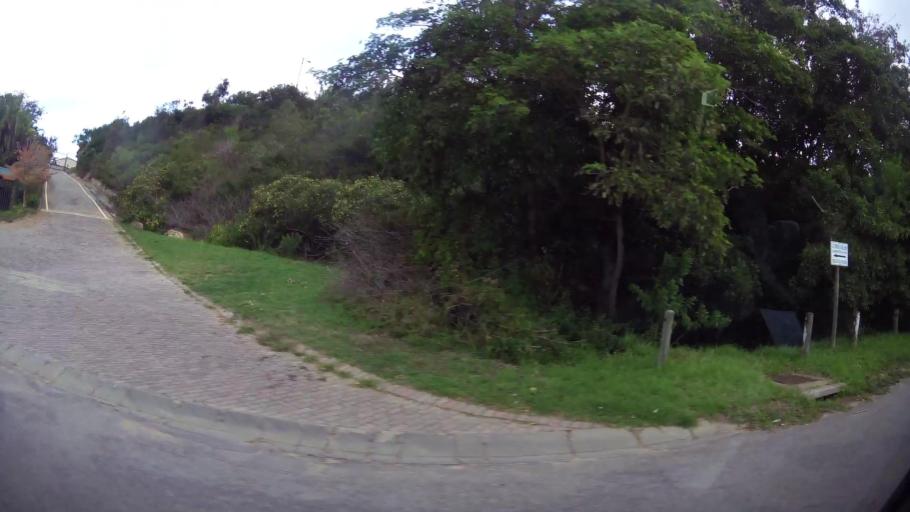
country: ZA
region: Western Cape
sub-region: Eden District Municipality
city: Plettenberg Bay
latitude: -34.0494
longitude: 23.3721
